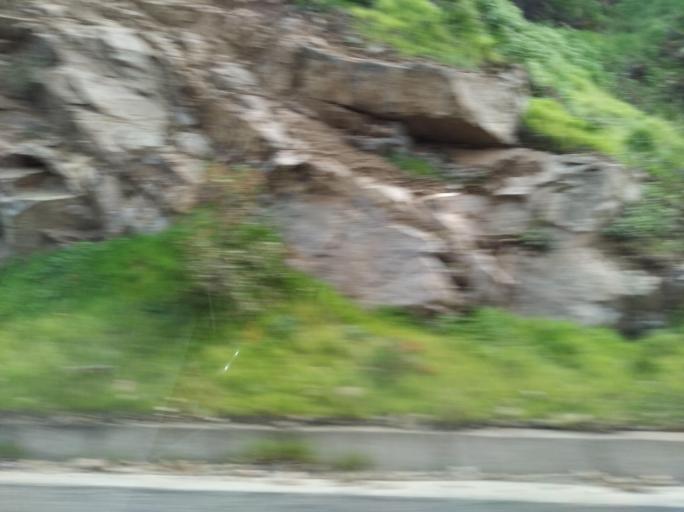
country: CL
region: Valparaiso
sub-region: Provincia de San Felipe
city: Llaillay
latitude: -33.0718
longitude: -70.9695
